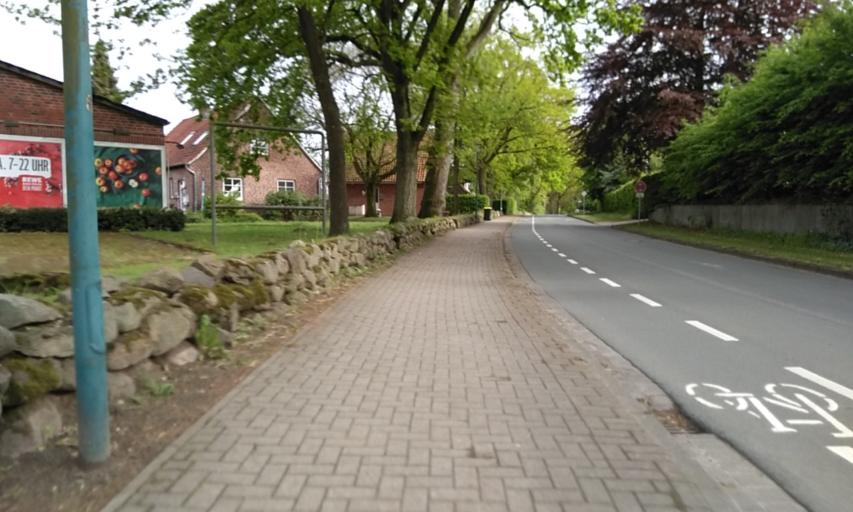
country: DE
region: Lower Saxony
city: Buxtehude
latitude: 53.4483
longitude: 9.6665
